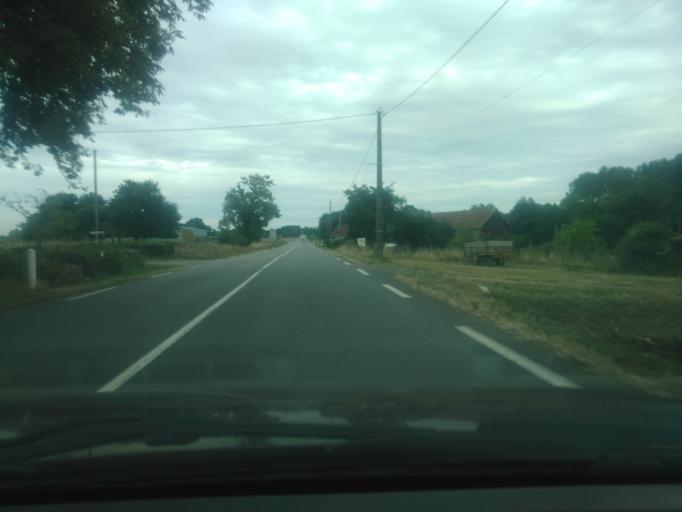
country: FR
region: Auvergne
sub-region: Departement de l'Allier
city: Ainay-le-Chateau
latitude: 46.7401
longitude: 2.7049
